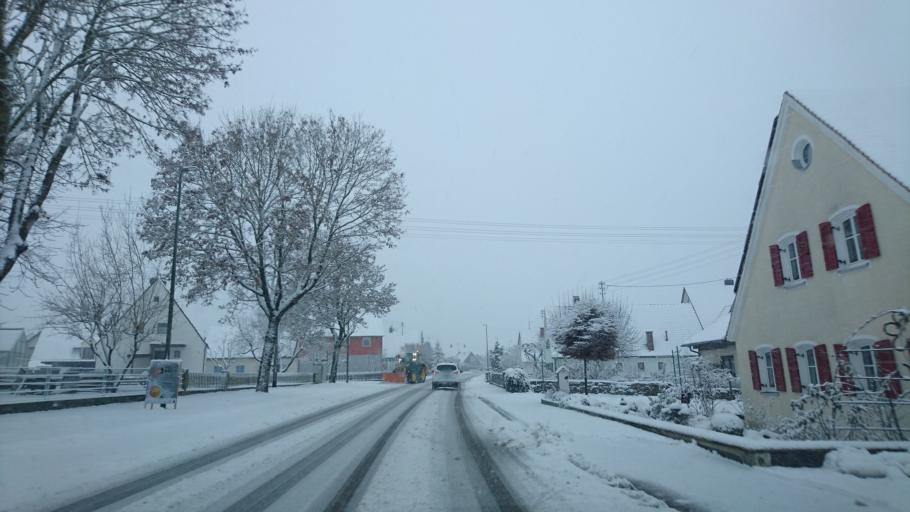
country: DE
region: Bavaria
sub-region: Swabia
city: Emersacker
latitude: 48.4941
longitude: 10.6743
